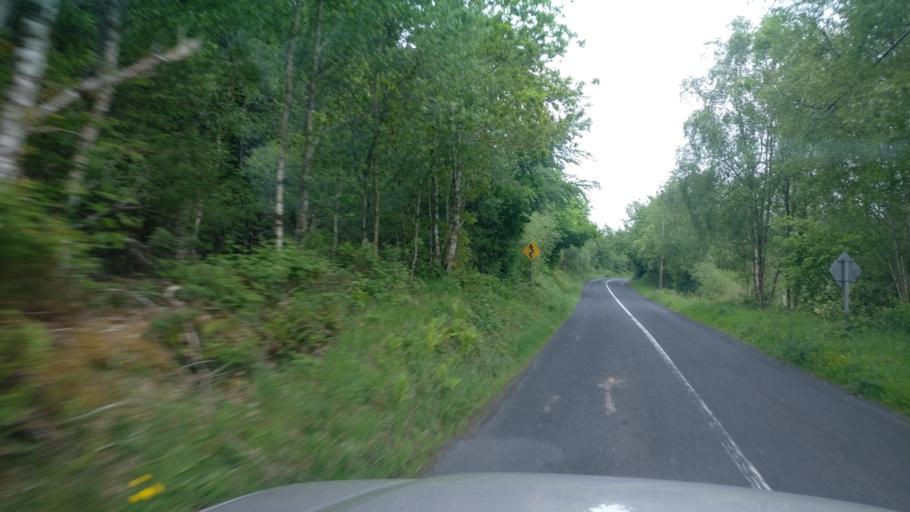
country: IE
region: Connaught
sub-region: County Galway
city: Gort
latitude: 53.0591
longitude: -8.6652
